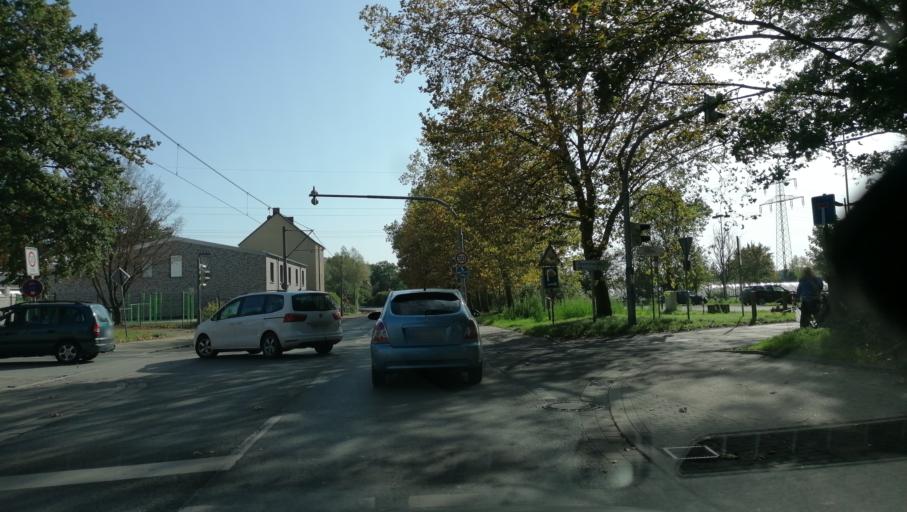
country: DE
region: North Rhine-Westphalia
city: Waltrop
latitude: 51.5898
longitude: 7.4412
